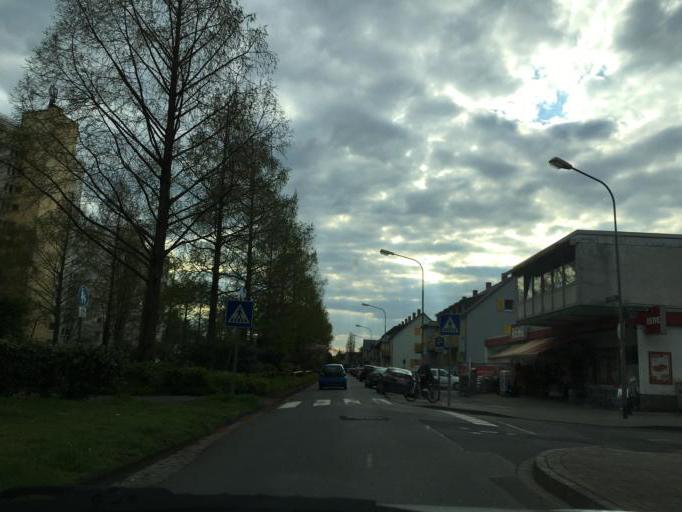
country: DE
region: Hesse
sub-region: Regierungsbezirk Darmstadt
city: Offenbach
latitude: 50.0986
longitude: 8.7789
